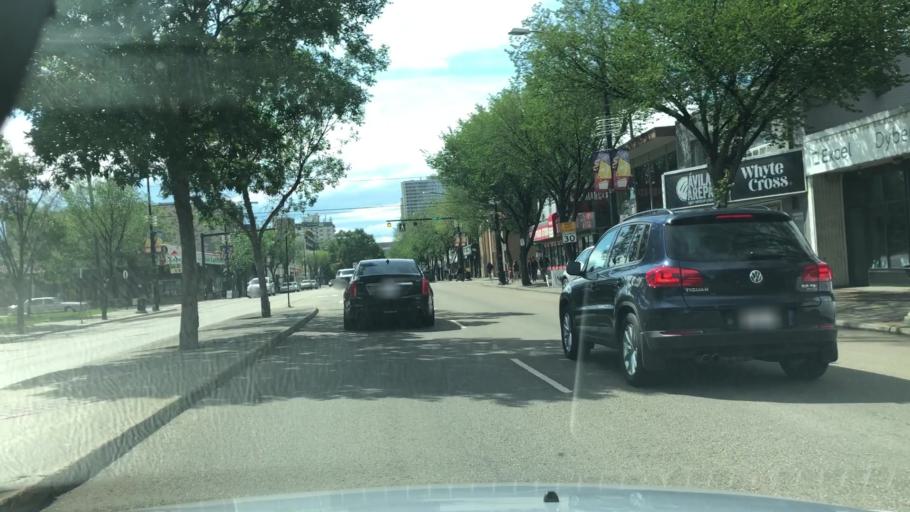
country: CA
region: Alberta
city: Edmonton
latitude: 53.5181
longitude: -113.5082
